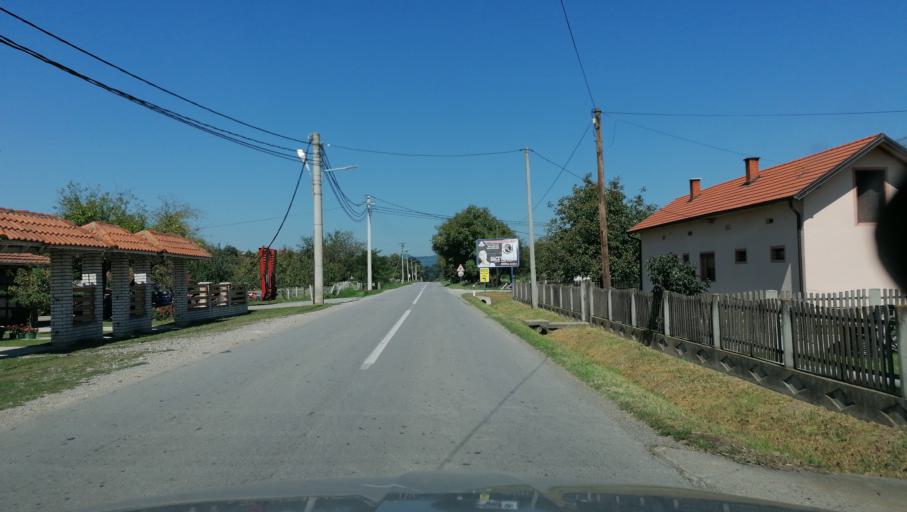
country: RS
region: Central Serbia
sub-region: Raski Okrug
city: Vrnjacka Banja
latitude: 43.7100
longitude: 20.8358
